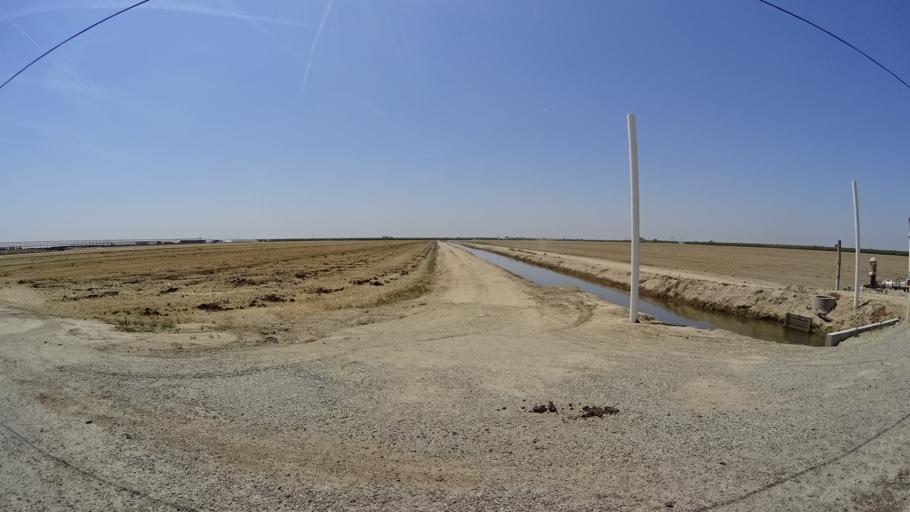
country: US
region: California
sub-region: Fresno County
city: Kingsburg
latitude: 36.4014
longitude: -119.5431
